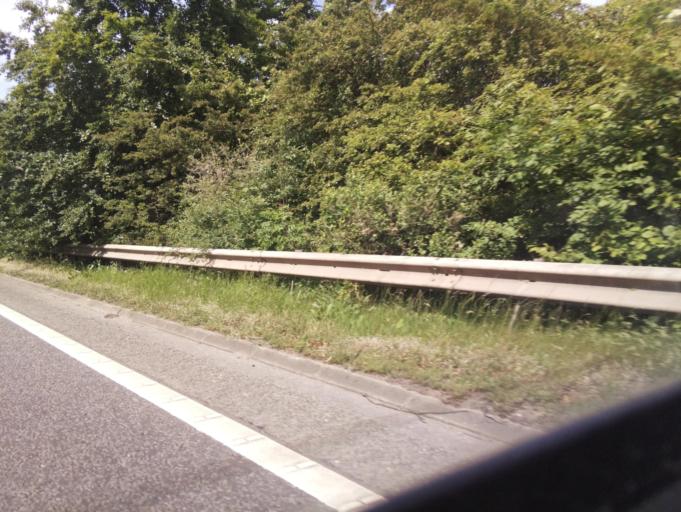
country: GB
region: England
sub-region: Lincolnshire
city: Burton
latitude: 53.2502
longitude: -0.5591
